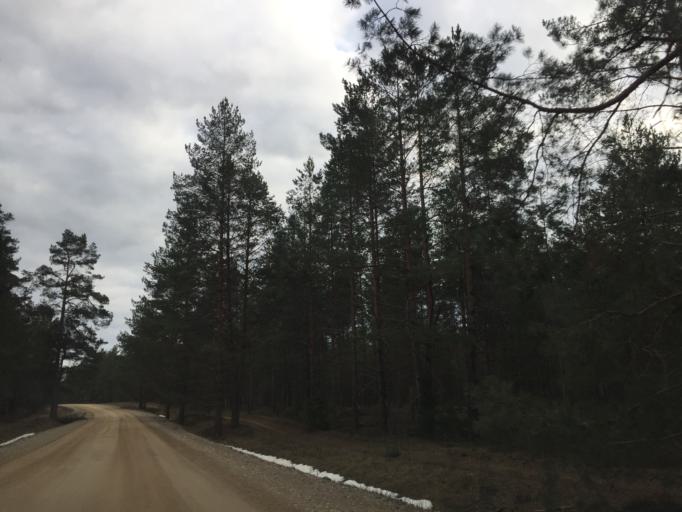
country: LV
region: Jaunjelgava
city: Jaunjelgava
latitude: 56.5749
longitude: 25.0116
